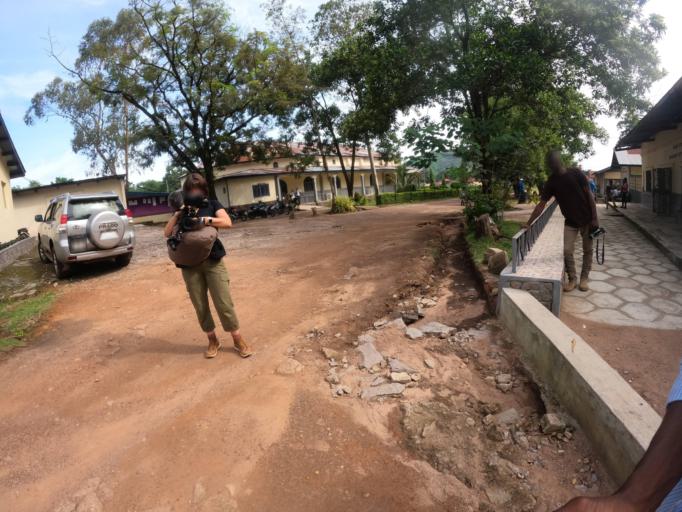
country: SL
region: Northern Province
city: Makeni
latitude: 8.8879
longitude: -12.0575
